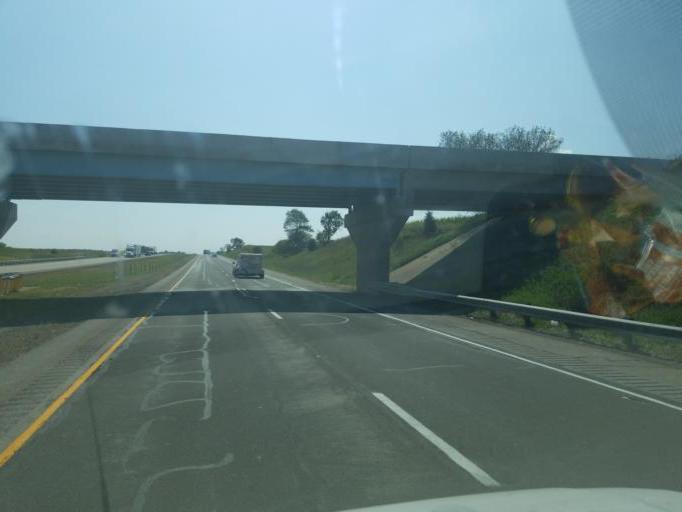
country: US
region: Indiana
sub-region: Steuben County
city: Angola
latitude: 41.5712
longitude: -85.0581
